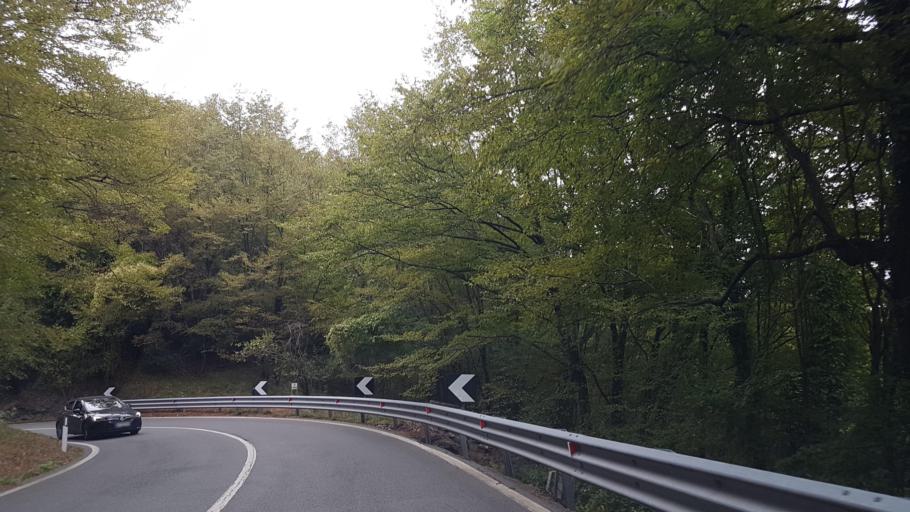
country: IT
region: Liguria
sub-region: Provincia di Genova
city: Castiglione
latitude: 44.2535
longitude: 9.5317
